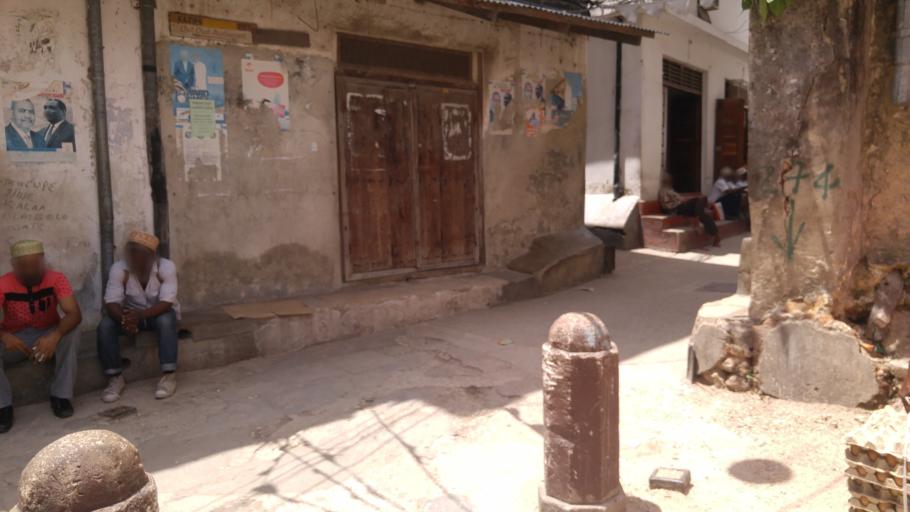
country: TZ
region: Zanzibar Urban/West
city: Zanzibar
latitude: -6.1634
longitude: 39.1907
